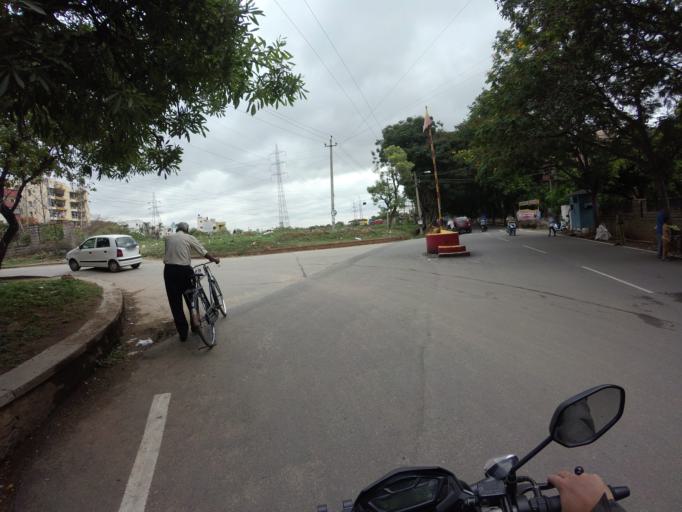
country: IN
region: Karnataka
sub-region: Bangalore Urban
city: Bangalore
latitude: 12.9712
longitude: 77.6669
